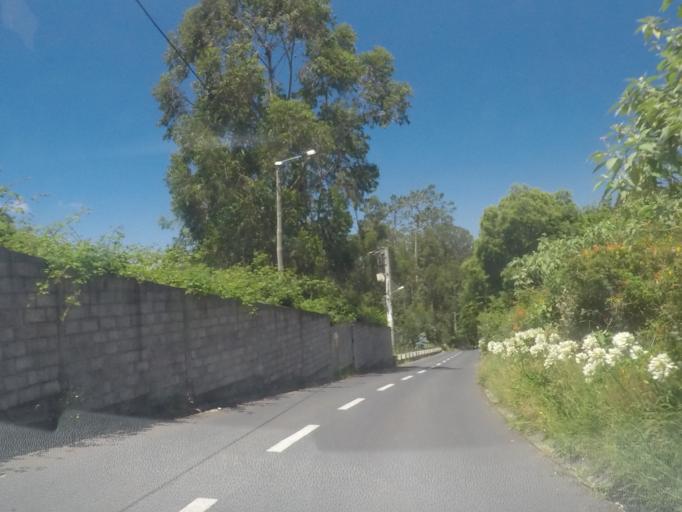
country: PT
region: Madeira
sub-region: Camara de Lobos
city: Curral das Freiras
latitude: 32.6868
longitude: -16.9788
